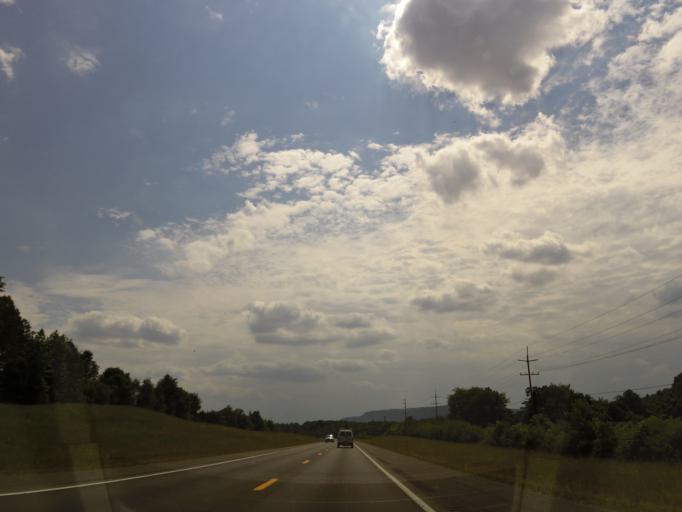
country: US
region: Tennessee
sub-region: Marion County
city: Jasper
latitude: 35.0969
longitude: -85.5899
